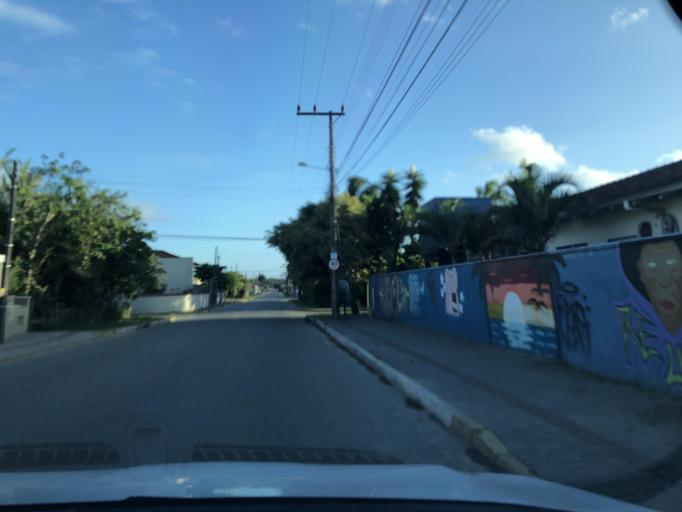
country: BR
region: Santa Catarina
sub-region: Sao Francisco Do Sul
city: Sao Francisco do Sul
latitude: -26.2300
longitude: -48.5247
